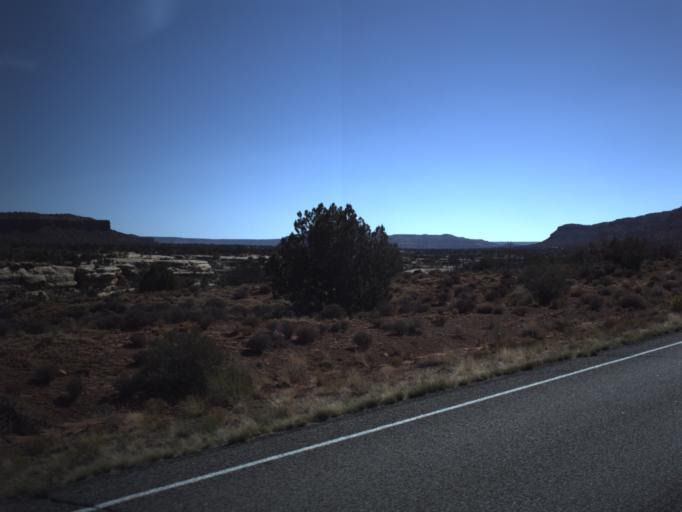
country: US
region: Utah
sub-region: San Juan County
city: Blanding
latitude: 37.6869
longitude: -110.2228
